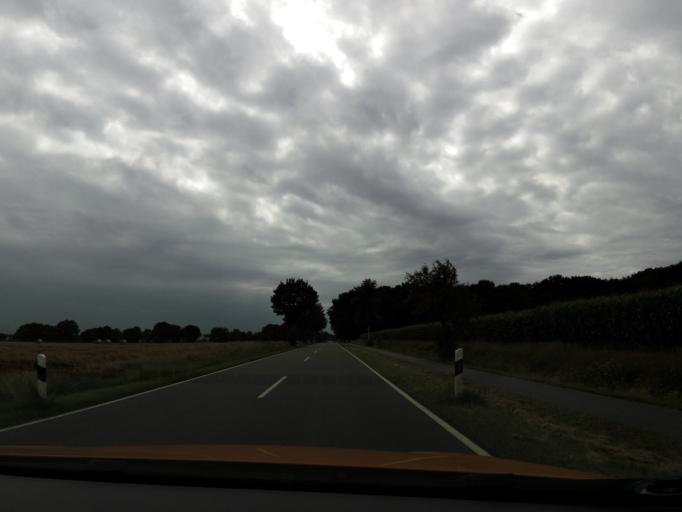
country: DE
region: Lower Saxony
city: Gross Ippener
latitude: 52.9845
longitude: 8.6148
